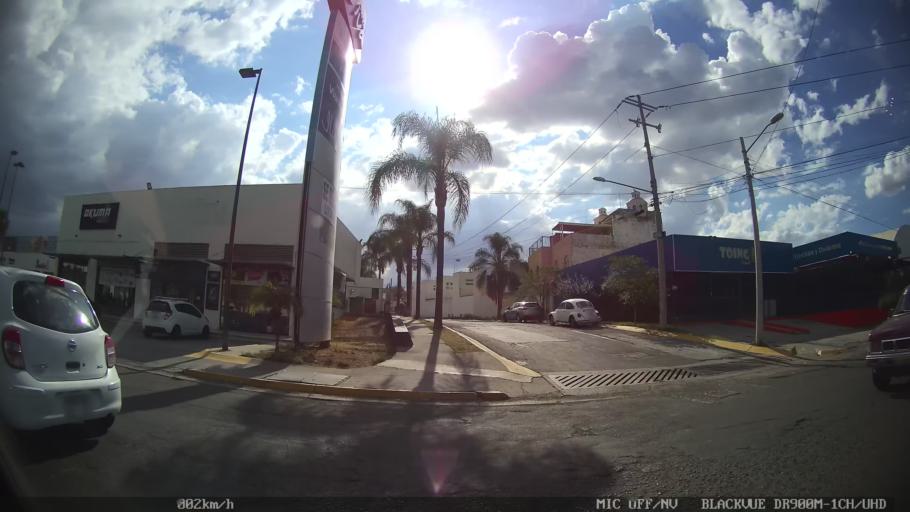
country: MX
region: Jalisco
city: Tlaquepaque
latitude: 20.6387
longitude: -103.2835
